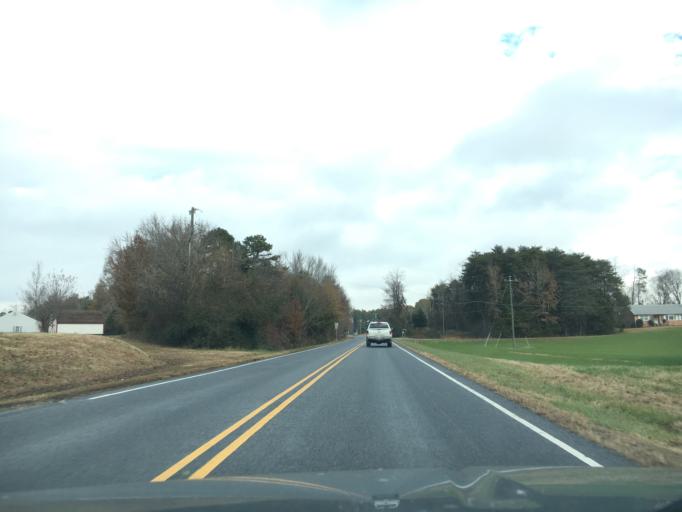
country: US
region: Virginia
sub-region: Prince Edward County
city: Farmville
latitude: 37.3423
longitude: -78.3883
